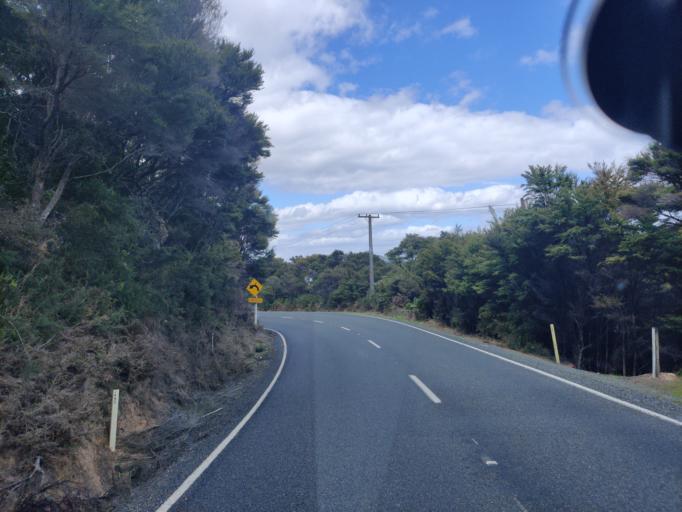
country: NZ
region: Northland
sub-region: Far North District
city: Paihia
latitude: -35.2616
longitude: 174.2185
